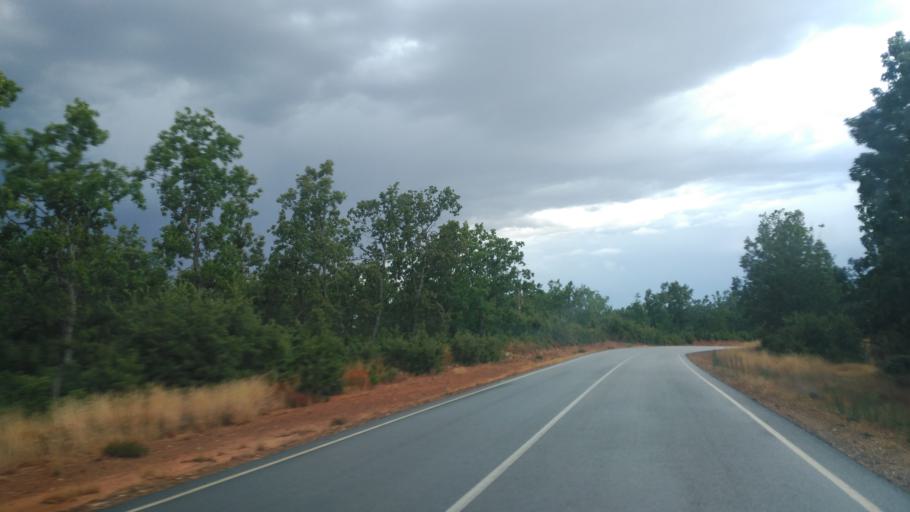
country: ES
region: Castille and Leon
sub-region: Provincia de Salamanca
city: Cereceda de la Sierra
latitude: 40.5785
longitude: -6.1308
